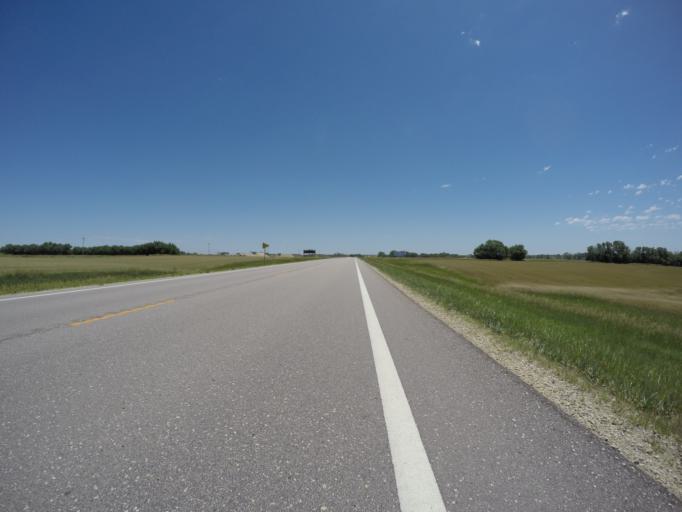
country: US
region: Kansas
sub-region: Republic County
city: Belleville
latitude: 39.8120
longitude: -97.7007
